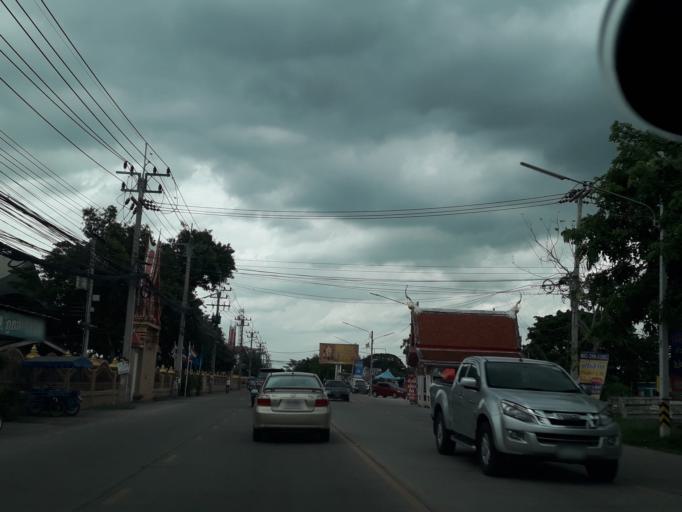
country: TH
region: Pathum Thani
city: Khlong Luang
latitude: 14.0492
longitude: 100.6635
